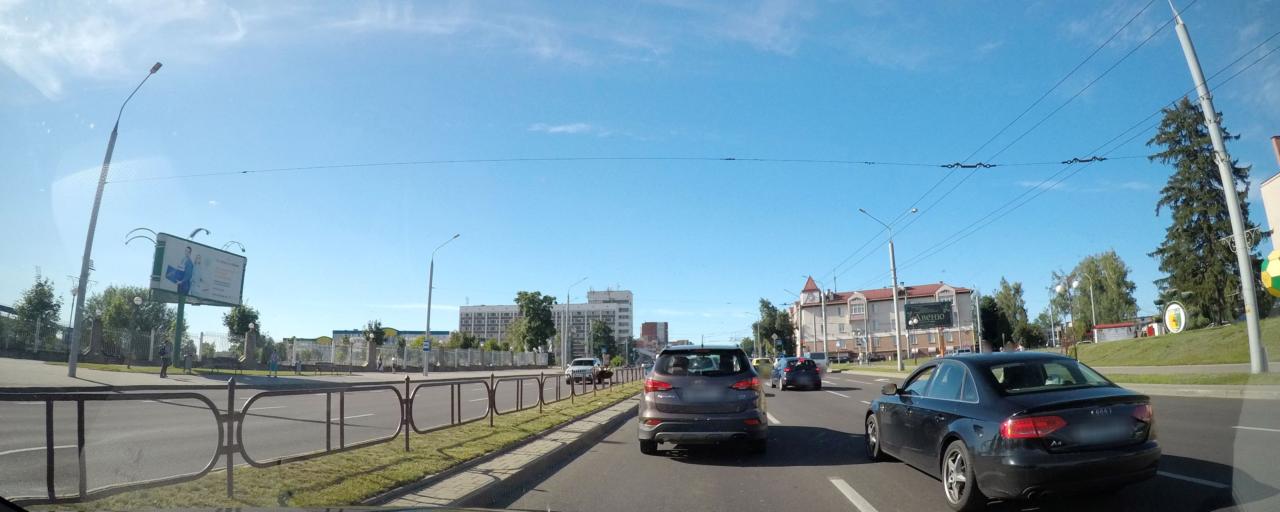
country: BY
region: Grodnenskaya
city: Hrodna
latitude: 53.6893
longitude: 23.8263
